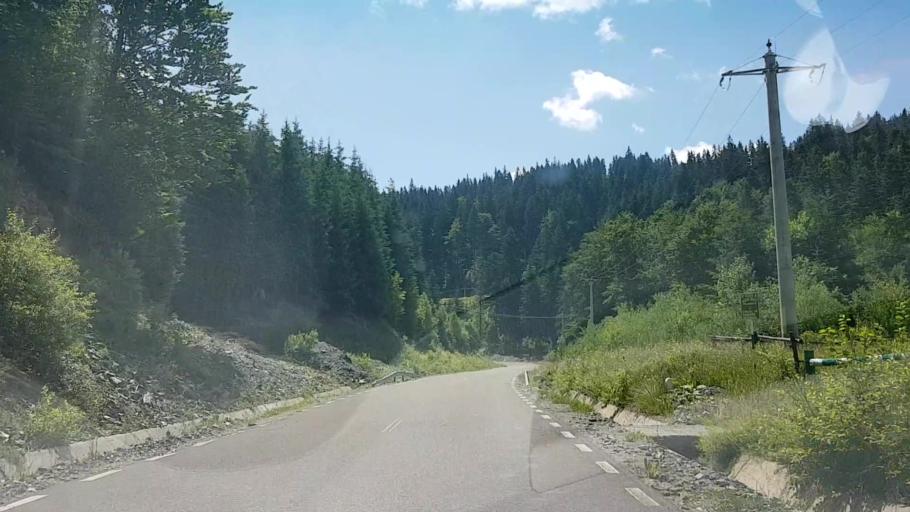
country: RO
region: Suceava
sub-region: Comuna Sadova
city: Sadova
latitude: 47.4659
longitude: 25.5152
